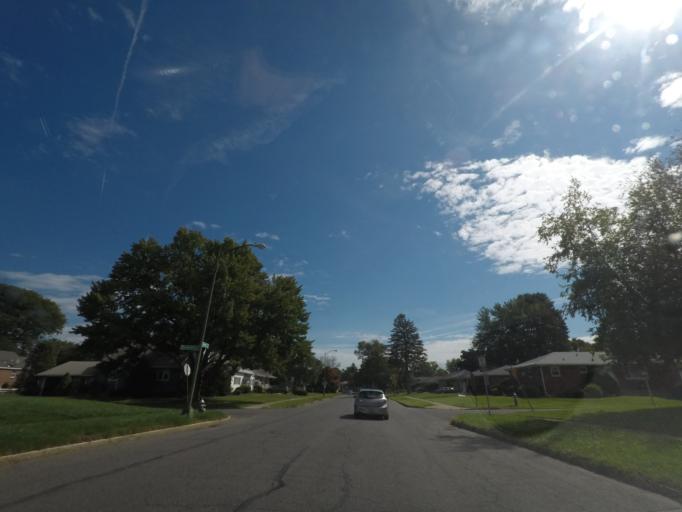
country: US
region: New York
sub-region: Albany County
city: Delmar
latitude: 42.6542
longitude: -73.8130
